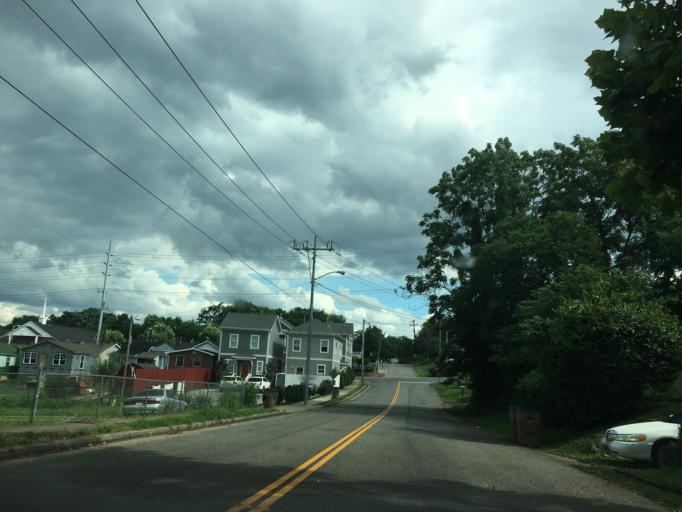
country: US
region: Tennessee
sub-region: Davidson County
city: Nashville
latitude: 36.1636
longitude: -86.8085
